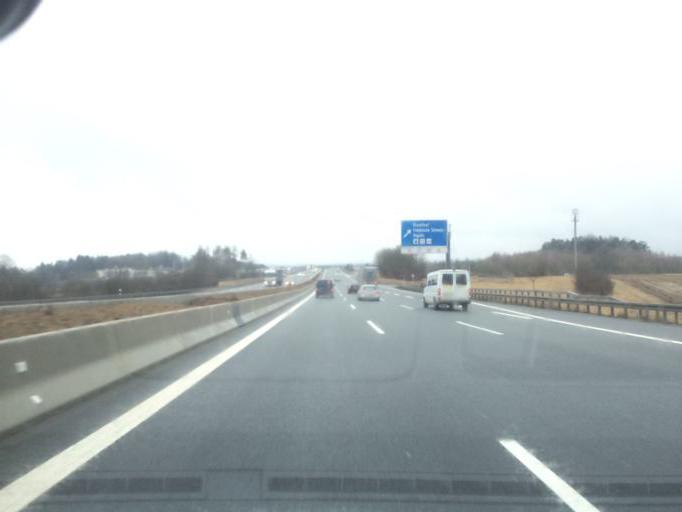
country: DE
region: Bavaria
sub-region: Upper Franconia
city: Pegnitz
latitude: 49.7547
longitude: 11.5098
